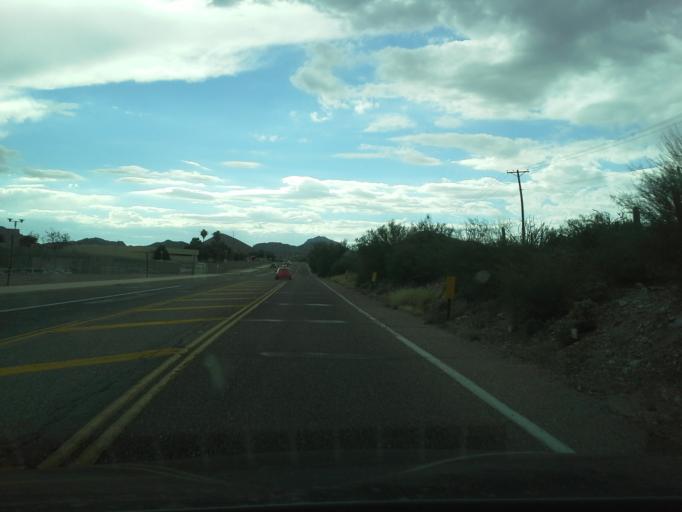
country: US
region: Arizona
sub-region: Pima County
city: South Tucson
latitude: 32.2069
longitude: -111.0077
